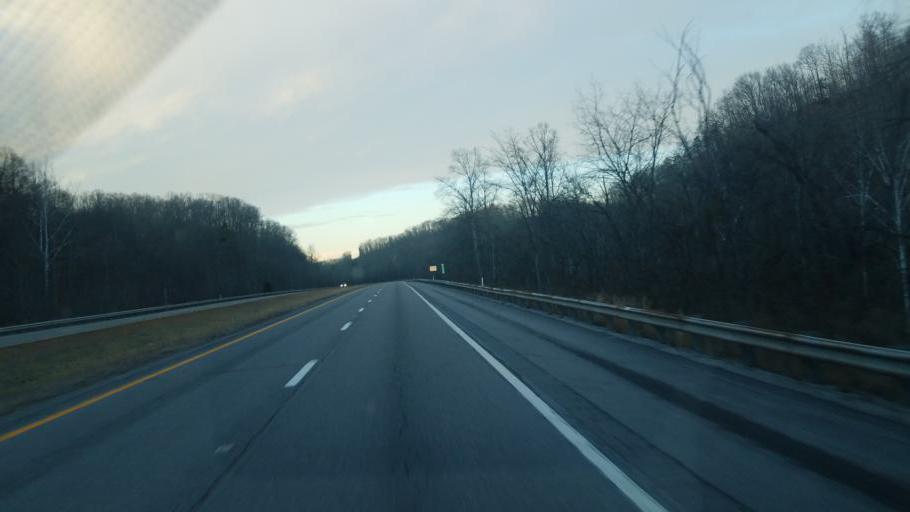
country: US
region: West Virginia
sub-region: Kanawha County
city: Sissonville
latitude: 38.6119
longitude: -81.6392
